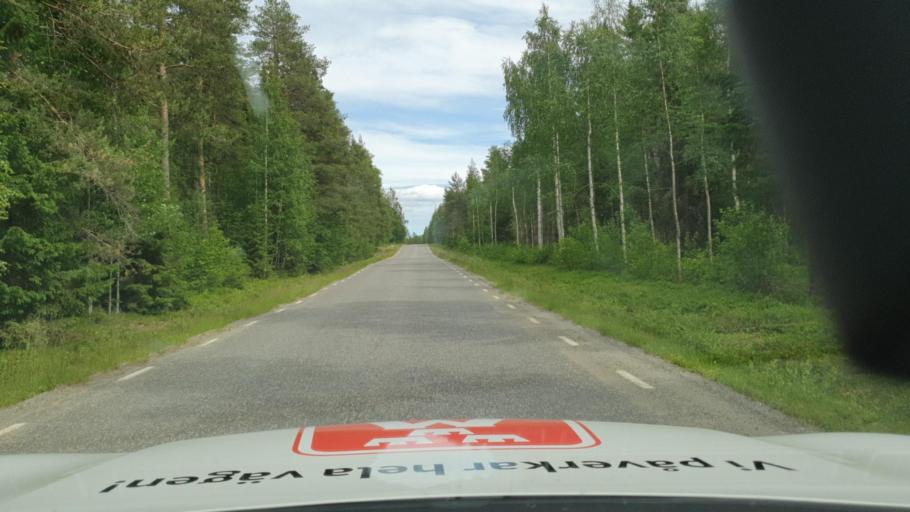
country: SE
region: Vaesterbotten
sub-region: Skelleftea Kommun
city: Viken
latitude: 64.4982
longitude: 20.8837
